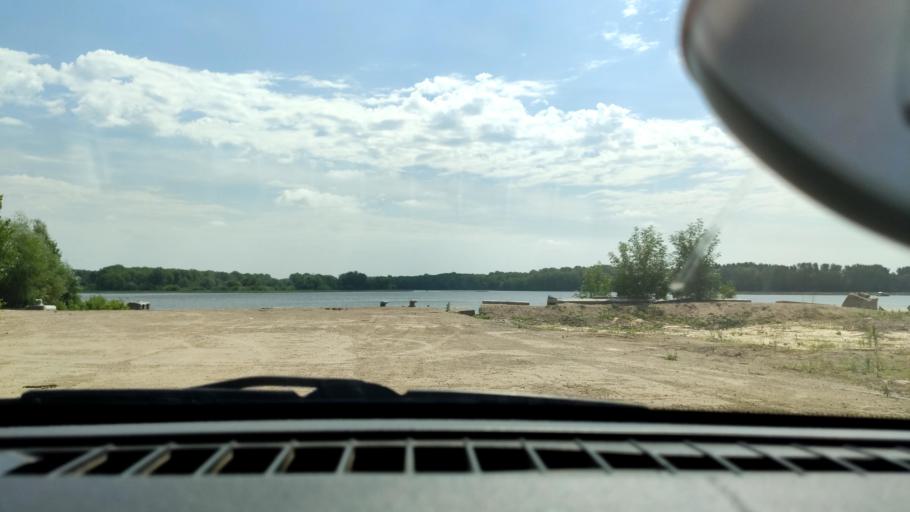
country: RU
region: Samara
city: Smyshlyayevka
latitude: 53.2034
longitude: 50.3223
